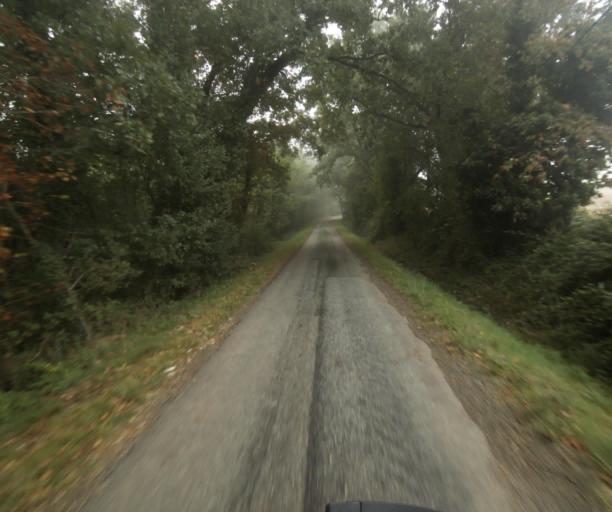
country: FR
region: Midi-Pyrenees
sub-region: Departement du Tarn-et-Garonne
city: Nohic
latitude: 43.9076
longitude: 1.4744
